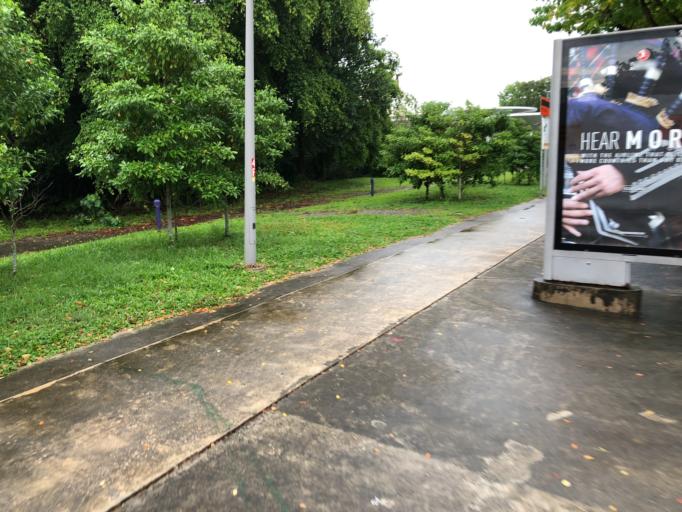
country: SG
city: Singapore
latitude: 1.2800
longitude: 103.8692
